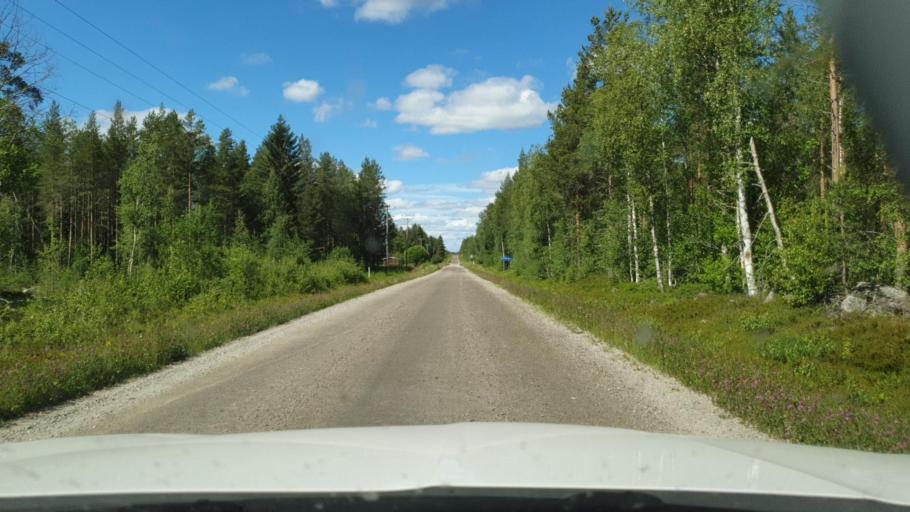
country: SE
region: Vaesterbotten
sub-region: Skelleftea Kommun
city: Backa
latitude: 65.1659
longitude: 21.1303
